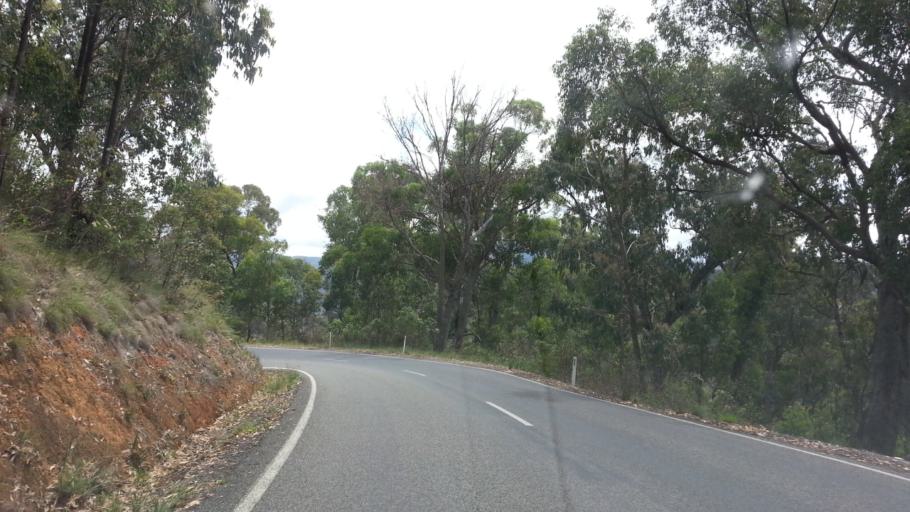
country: AU
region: Victoria
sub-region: Alpine
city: Mount Beauty
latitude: -36.7417
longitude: 147.1916
